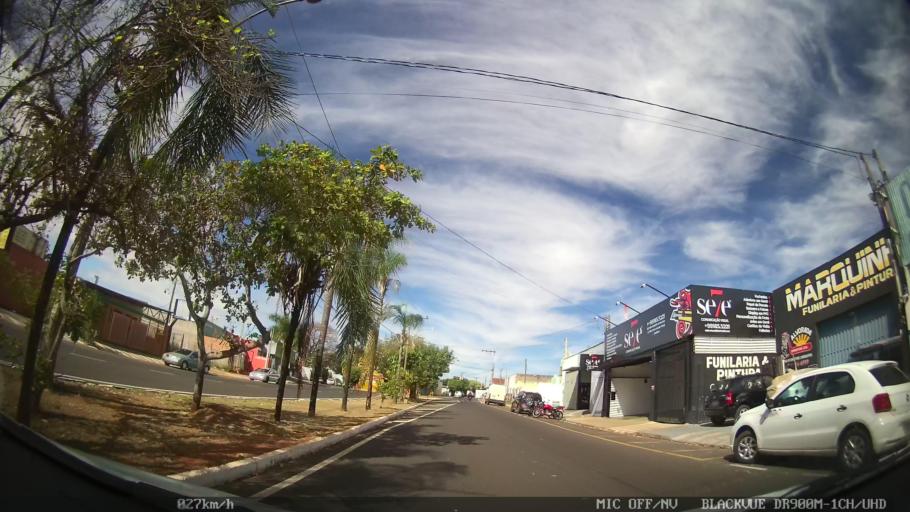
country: BR
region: Sao Paulo
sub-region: Sao Jose Do Rio Preto
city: Sao Jose do Rio Preto
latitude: -20.8410
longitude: -49.3426
